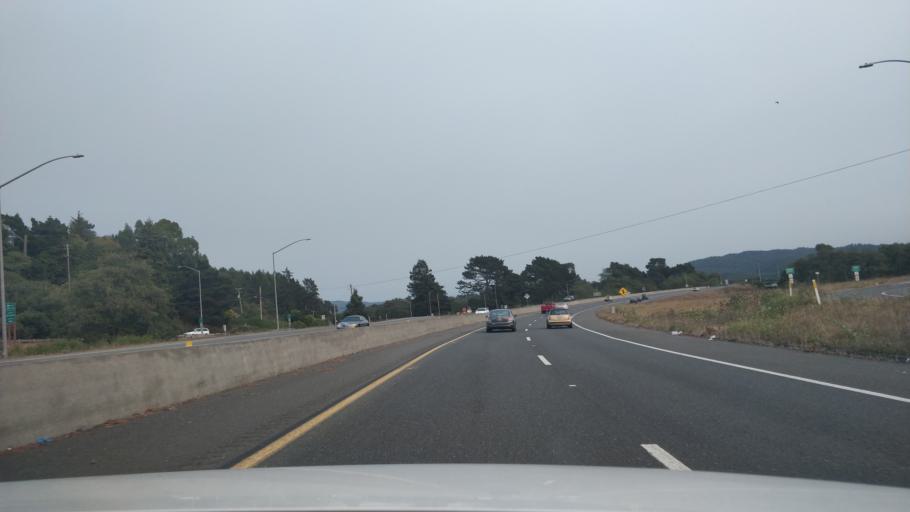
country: US
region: California
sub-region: Humboldt County
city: McKinleyville
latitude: 40.9203
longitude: -124.0970
